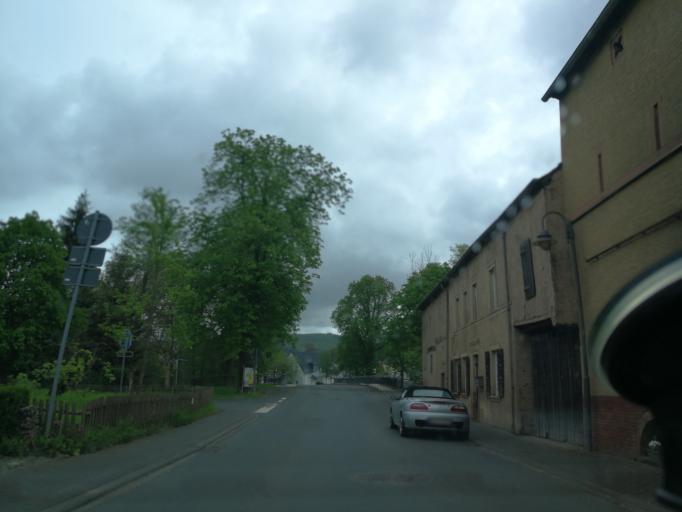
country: DE
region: Rheinland-Pfalz
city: Platten
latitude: 49.9492
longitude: 6.9515
